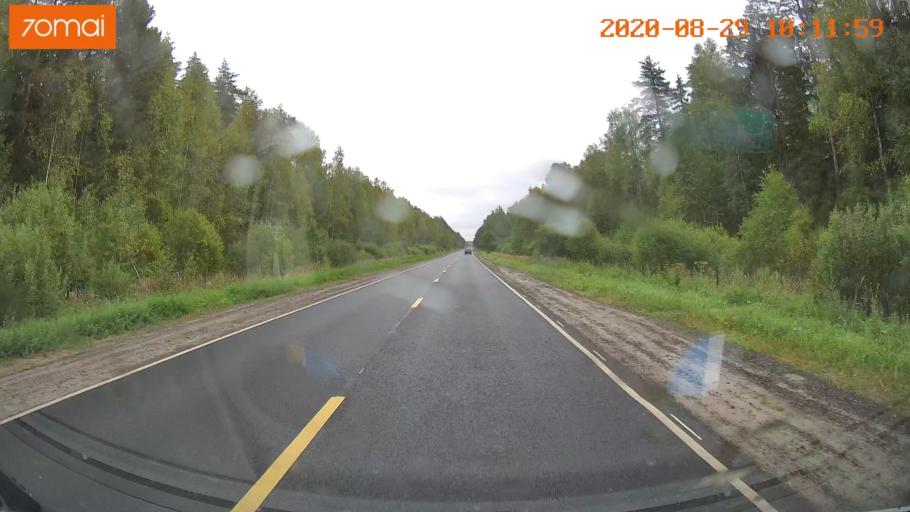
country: RU
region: Ivanovo
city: Kuznechikha
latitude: 57.3738
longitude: 42.6983
